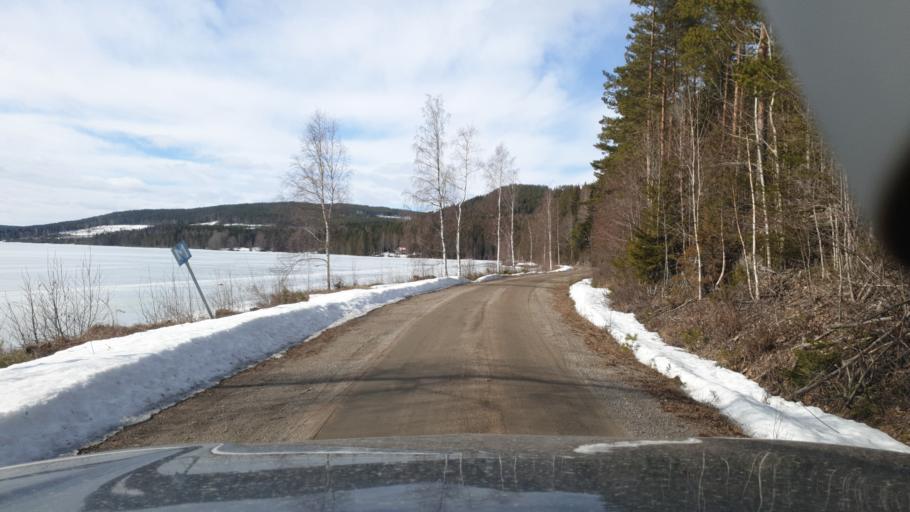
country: SE
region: Gaevleborg
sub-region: Ljusdals Kommun
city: Farila
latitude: 61.8467
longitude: 15.9199
